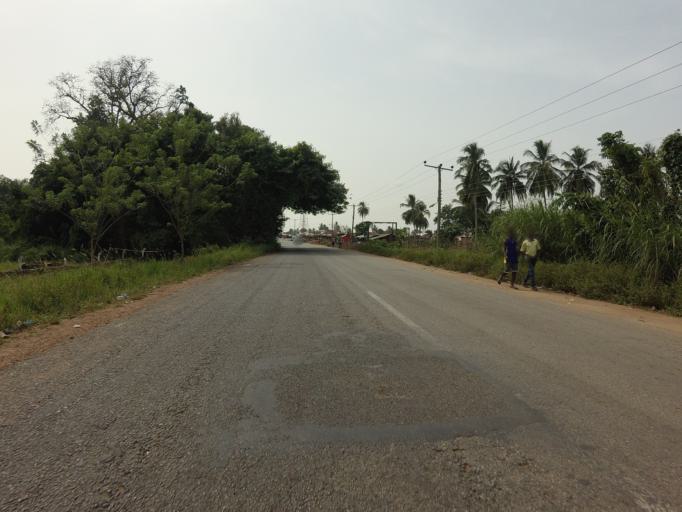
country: GH
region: Volta
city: Ho
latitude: 6.4101
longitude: 0.1725
